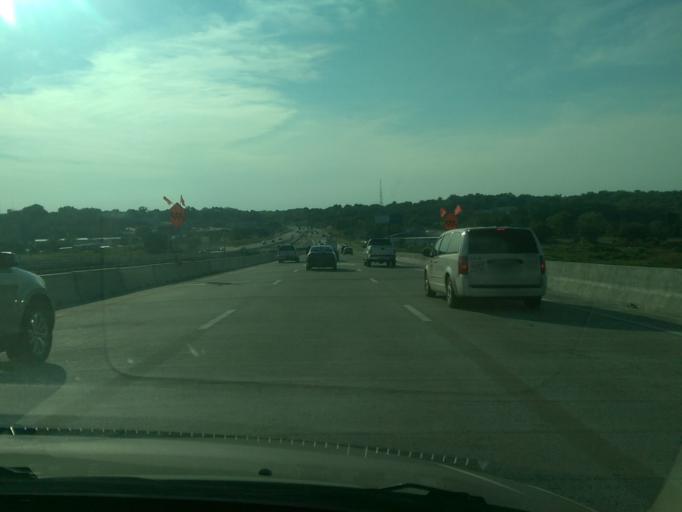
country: US
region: Missouri
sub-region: Jackson County
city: Raytown
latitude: 39.0664
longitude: -94.5053
